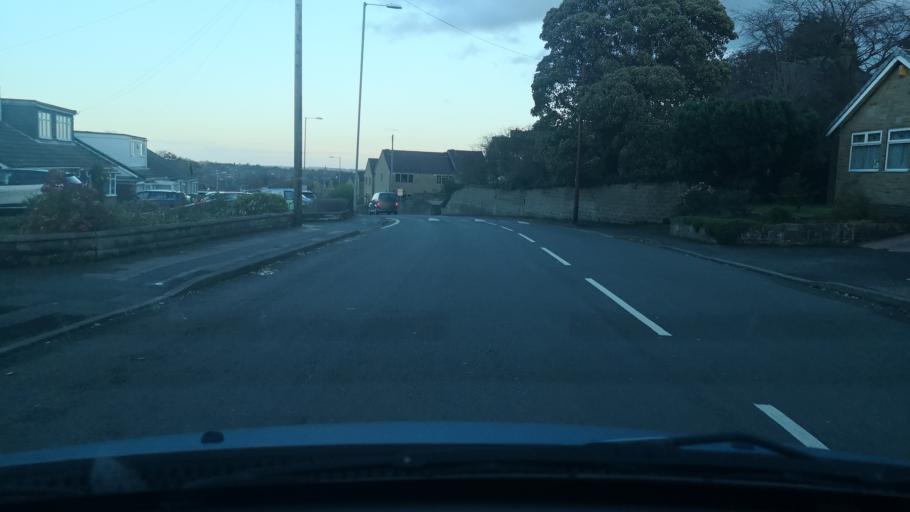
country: GB
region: England
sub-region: City and Borough of Wakefield
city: Middlestown
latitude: 53.6465
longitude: -1.5776
